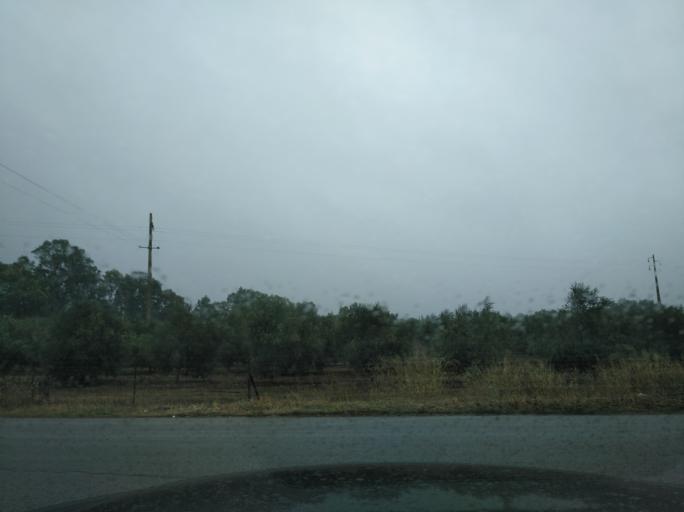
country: PT
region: Portalegre
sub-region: Campo Maior
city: Campo Maior
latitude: 38.9496
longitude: -7.0875
